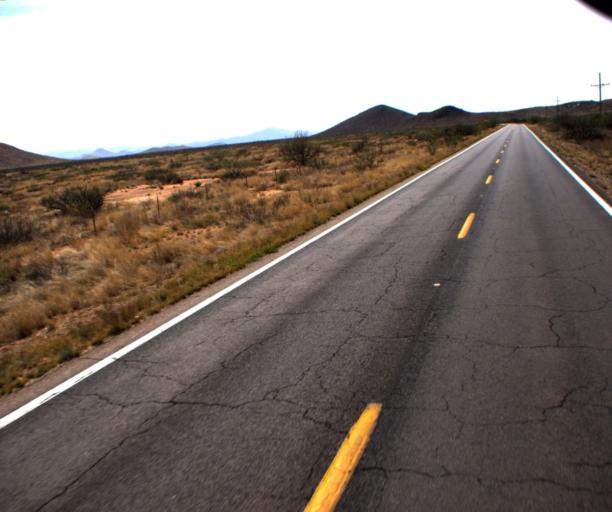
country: US
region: Arizona
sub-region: Cochise County
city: Tombstone
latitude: 31.9140
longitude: -109.8178
